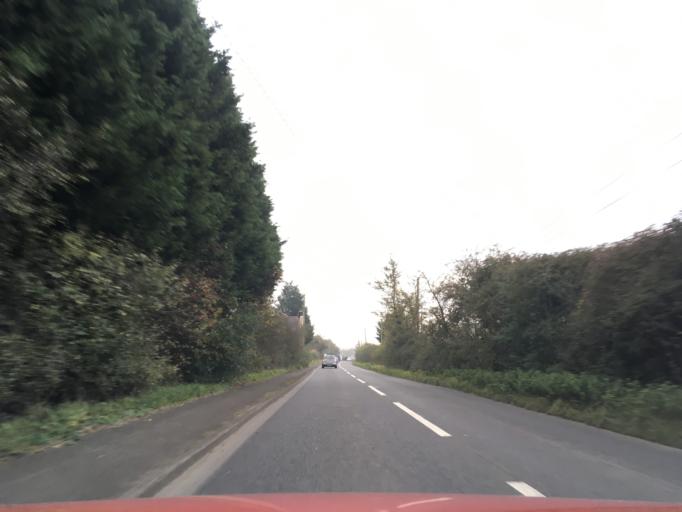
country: GB
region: England
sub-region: South Gloucestershire
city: Pucklechurch
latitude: 51.4947
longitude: -2.4318
